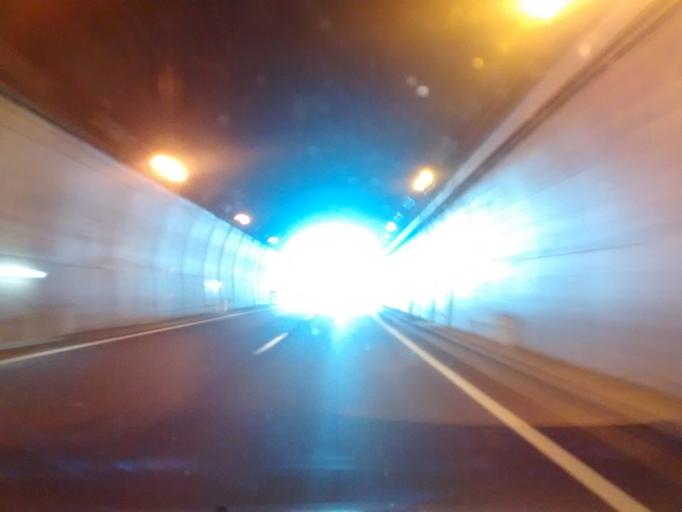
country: ES
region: Basque Country
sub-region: Provincia de Guipuzcoa
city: Deba
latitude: 43.2768
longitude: -2.3645
